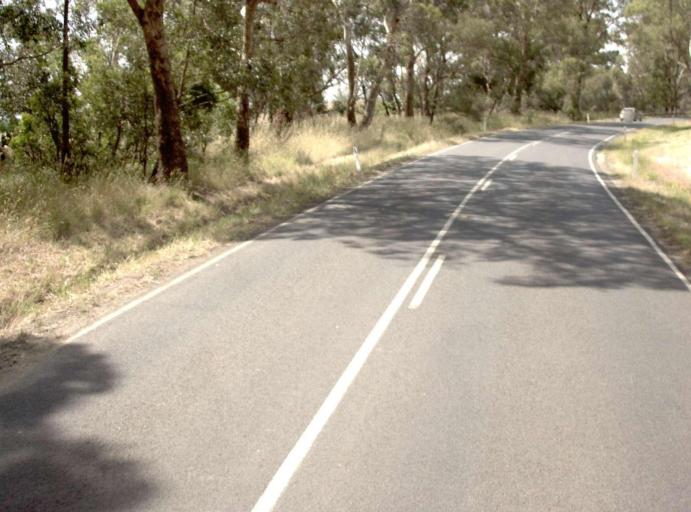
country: AU
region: Victoria
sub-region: Latrobe
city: Traralgon
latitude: -38.2606
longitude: 146.5468
